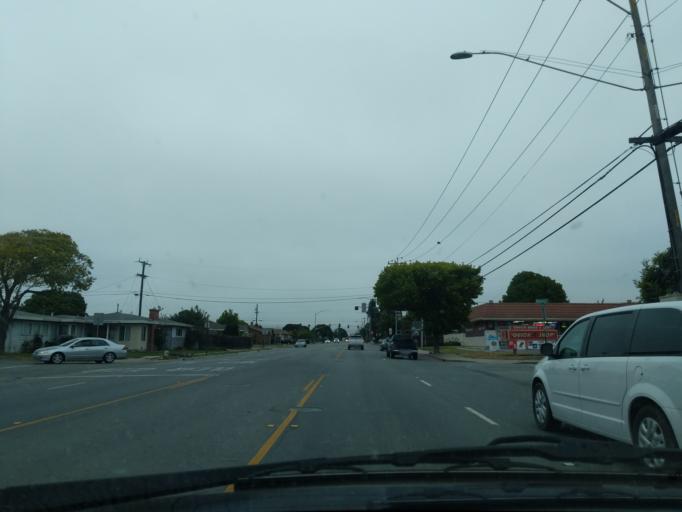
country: US
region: California
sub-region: Monterey County
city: Boronda
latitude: 36.6981
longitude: -121.6617
